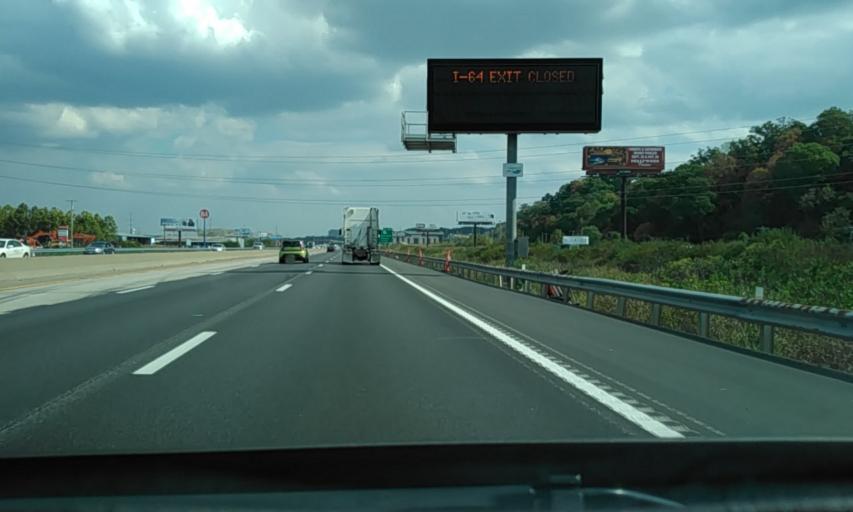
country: US
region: Missouri
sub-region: Saint Louis County
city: Valley Park
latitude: 38.5367
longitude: -90.5096
